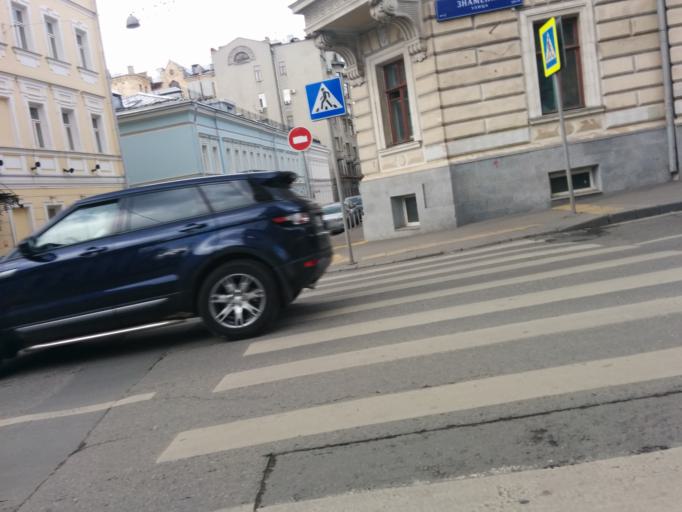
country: RU
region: Moscow
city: Moscow
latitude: 55.7498
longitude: 37.6067
